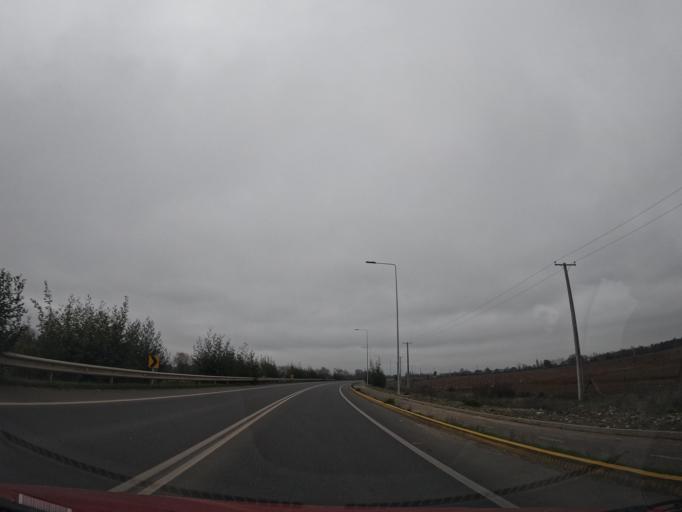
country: CL
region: Maule
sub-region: Provincia de Talca
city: San Clemente
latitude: -35.5097
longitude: -71.5091
